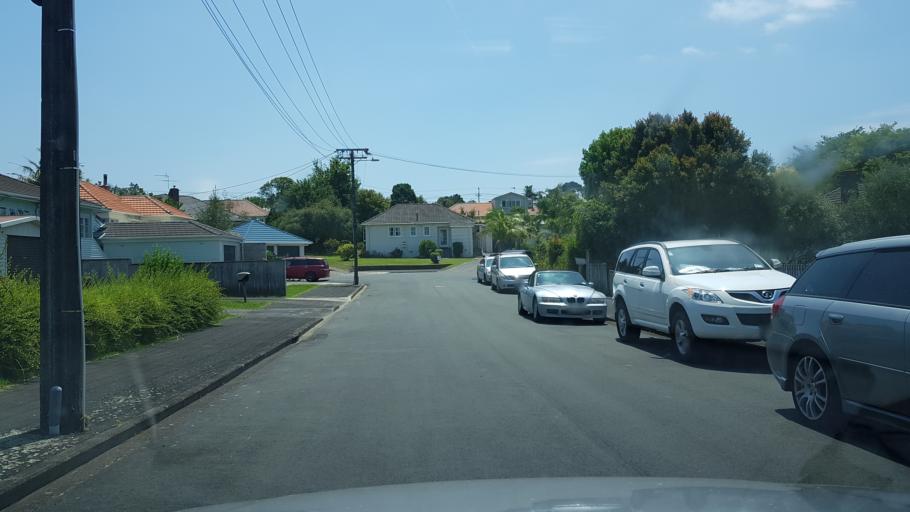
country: NZ
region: Auckland
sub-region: Auckland
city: North Shore
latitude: -36.8138
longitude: 174.7949
